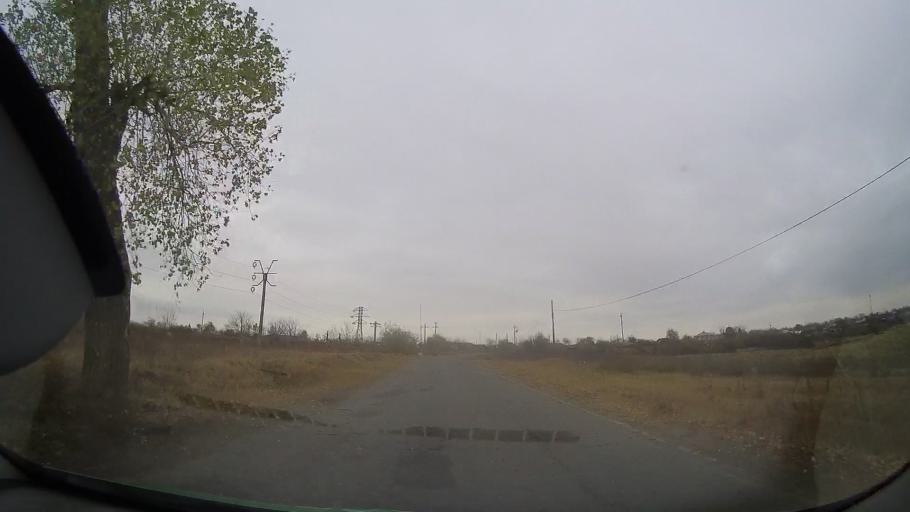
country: RO
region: Buzau
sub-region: Comuna Rusetu
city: Rusetu
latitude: 44.9527
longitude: 27.2198
